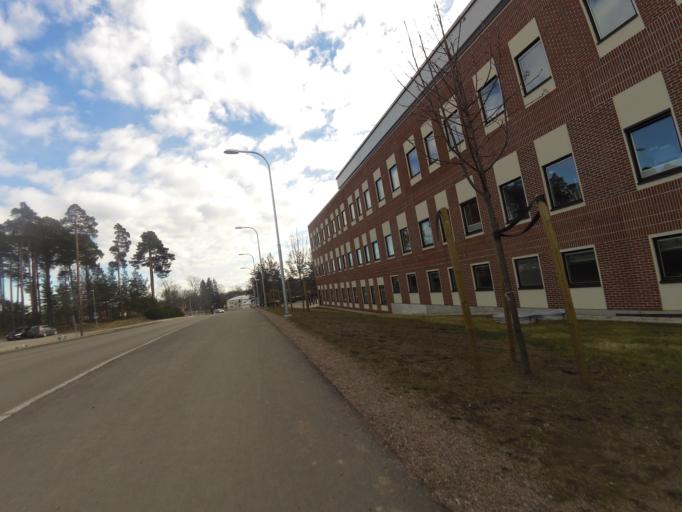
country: SE
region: Gaevleborg
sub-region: Gavle Kommun
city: Gavle
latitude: 60.6793
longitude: 17.1193
